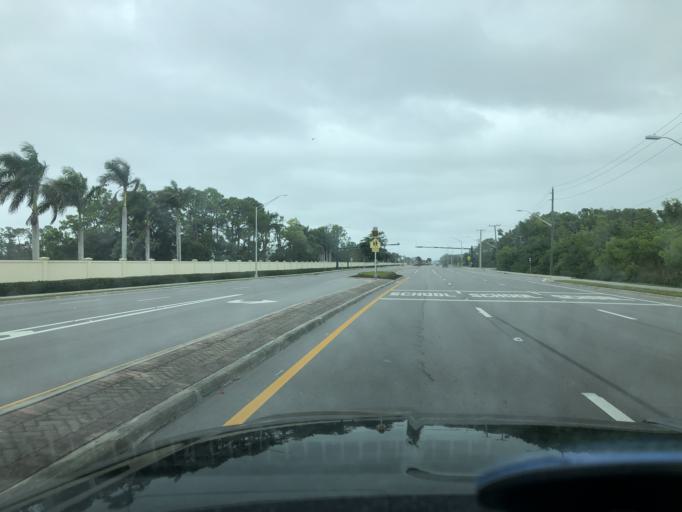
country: US
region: Florida
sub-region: Collier County
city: Lely
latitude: 26.1449
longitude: -81.7185
